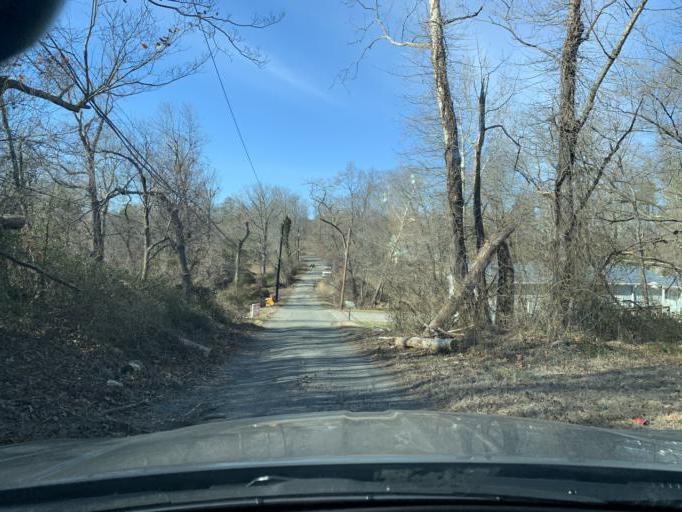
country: US
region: Maryland
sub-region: Prince George's County
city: Beltsville
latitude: 39.0653
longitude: -76.8962
